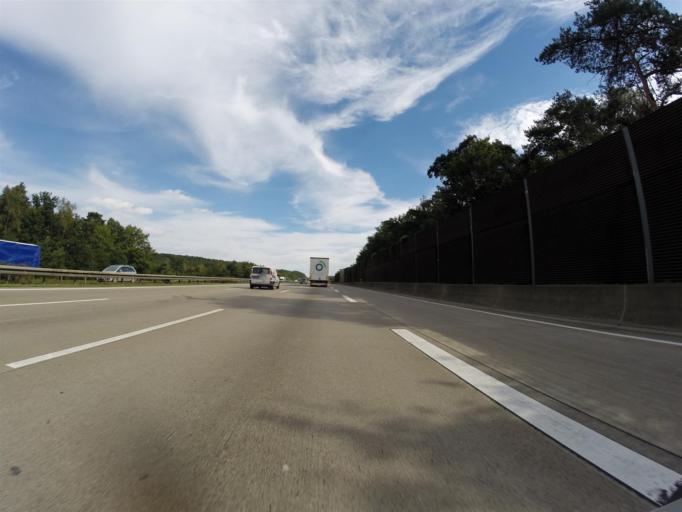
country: DE
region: Saxony
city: Radebeul
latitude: 51.1006
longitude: 13.7119
